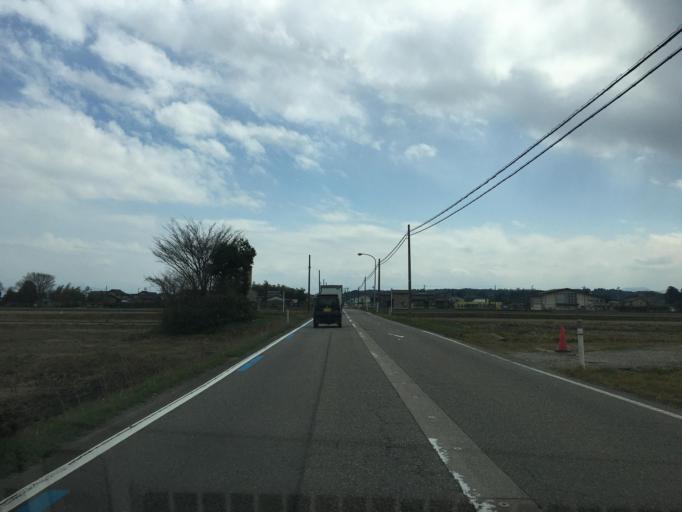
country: JP
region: Toyama
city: Kuragaki-kosugi
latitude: 36.6918
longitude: 137.1169
